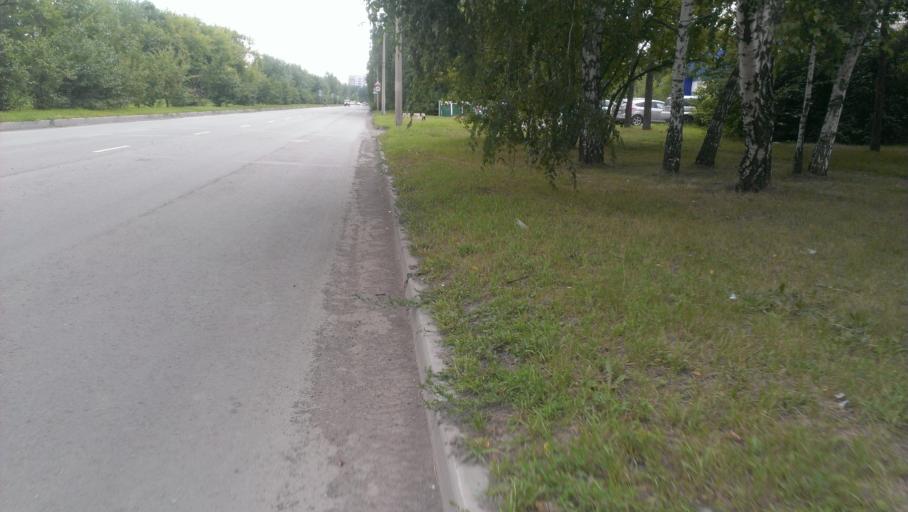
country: RU
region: Altai Krai
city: Yuzhnyy
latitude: 53.2531
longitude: 83.6977
